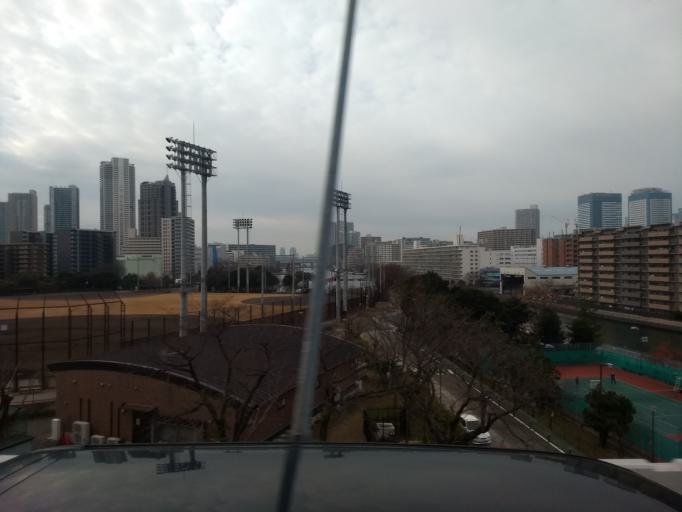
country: JP
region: Tokyo
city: Urayasu
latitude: 35.6563
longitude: 139.8106
